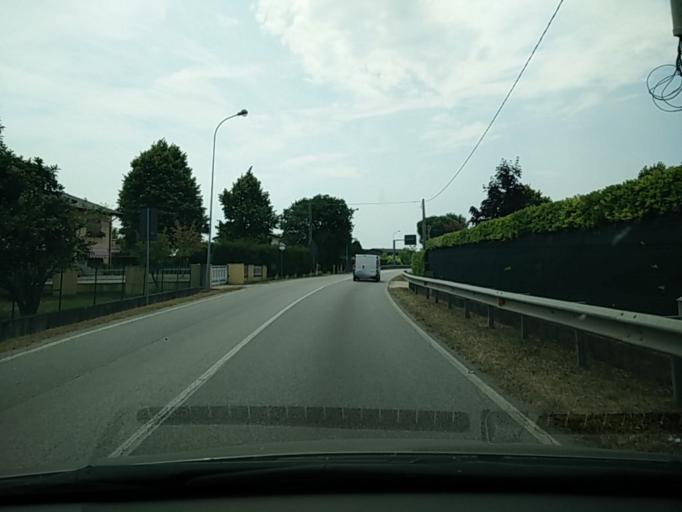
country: IT
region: Veneto
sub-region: Provincia di Treviso
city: Varago
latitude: 45.7382
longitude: 12.2878
